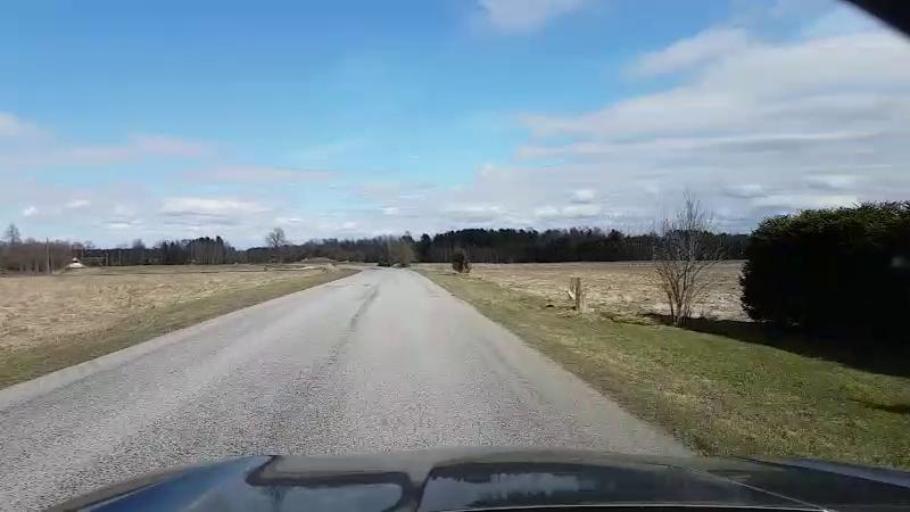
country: EE
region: Harju
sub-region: Saue linn
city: Saue
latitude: 59.3087
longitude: 24.5884
